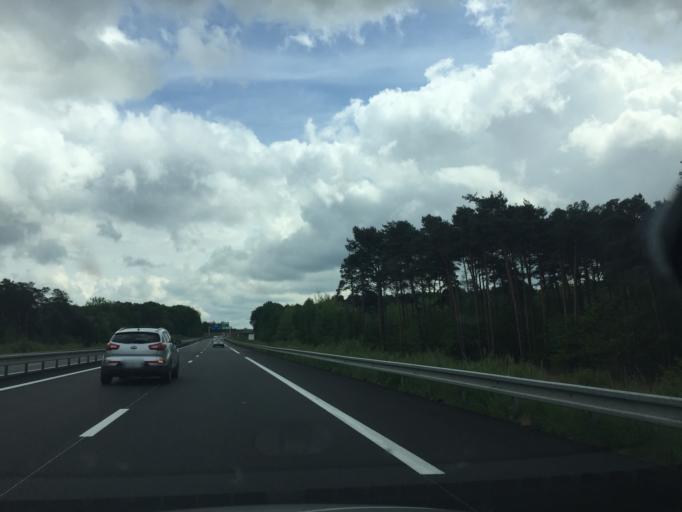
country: FR
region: Pays de la Loire
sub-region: Departement de la Sarthe
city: Champagne
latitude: 48.0056
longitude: 0.3060
